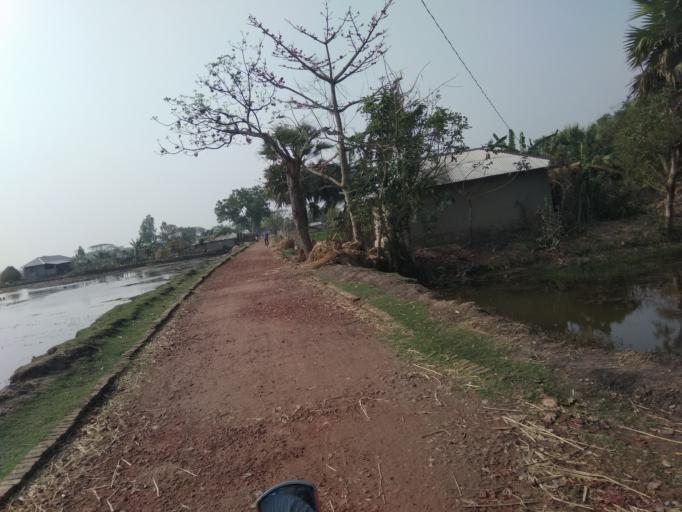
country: IN
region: West Bengal
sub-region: North 24 Parganas
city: Gosaba
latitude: 22.2640
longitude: 89.1155
